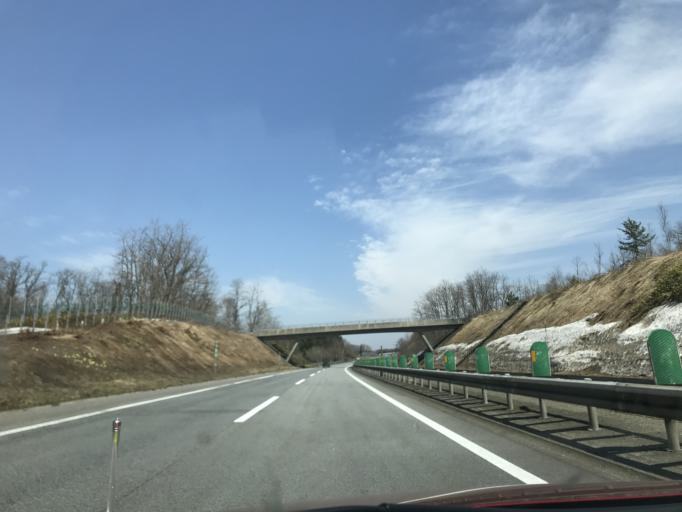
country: JP
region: Hokkaido
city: Bibai
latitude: 43.2563
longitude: 141.8331
